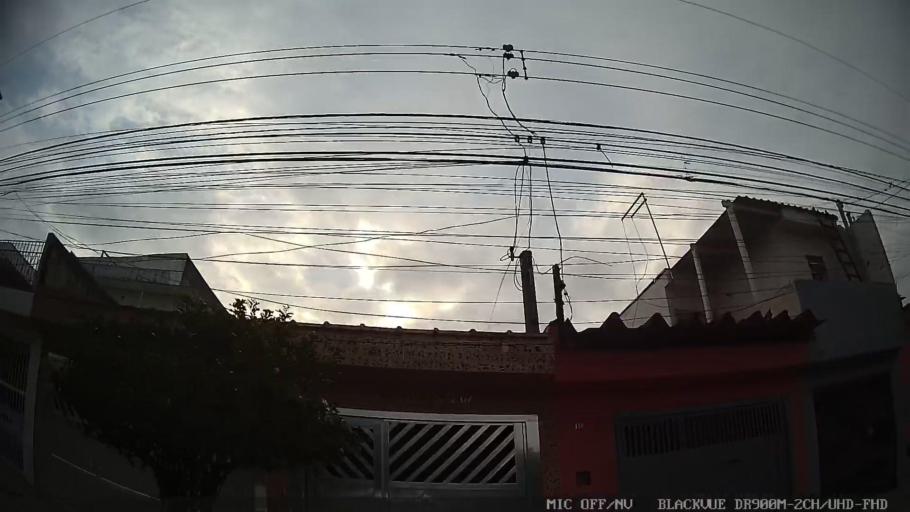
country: BR
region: Sao Paulo
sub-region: Itaquaquecetuba
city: Itaquaquecetuba
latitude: -23.4912
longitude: -46.4142
